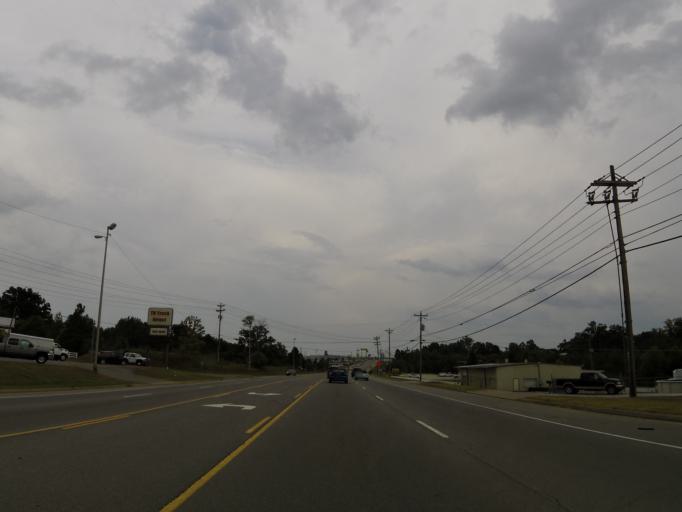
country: US
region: Tennessee
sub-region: Dickson County
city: Burns
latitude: 36.0285
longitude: -87.3460
